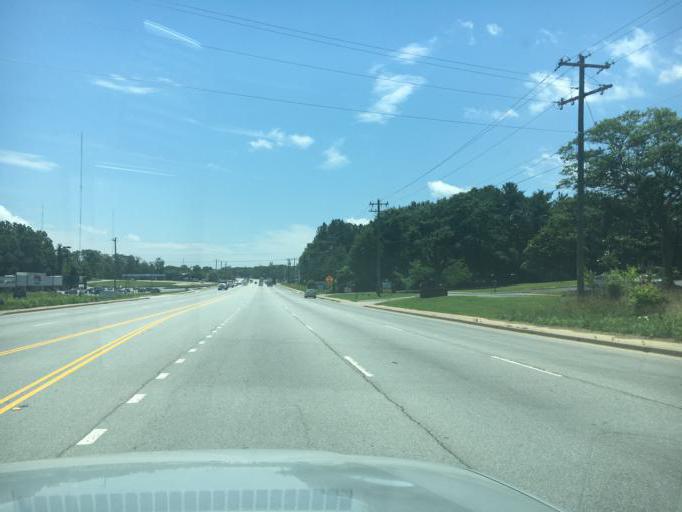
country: US
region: South Carolina
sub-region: Greenville County
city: Berea
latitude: 34.8938
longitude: -82.4676
